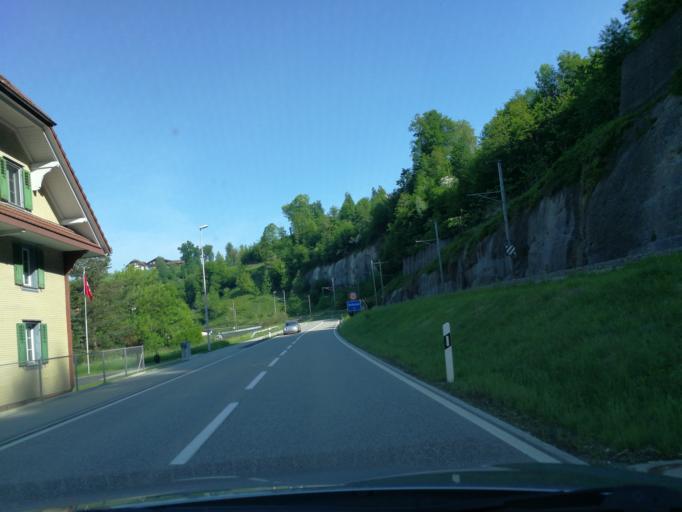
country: CH
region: Lucerne
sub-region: Entlebuch District
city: Werthenstein
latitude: 47.0547
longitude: 8.1050
